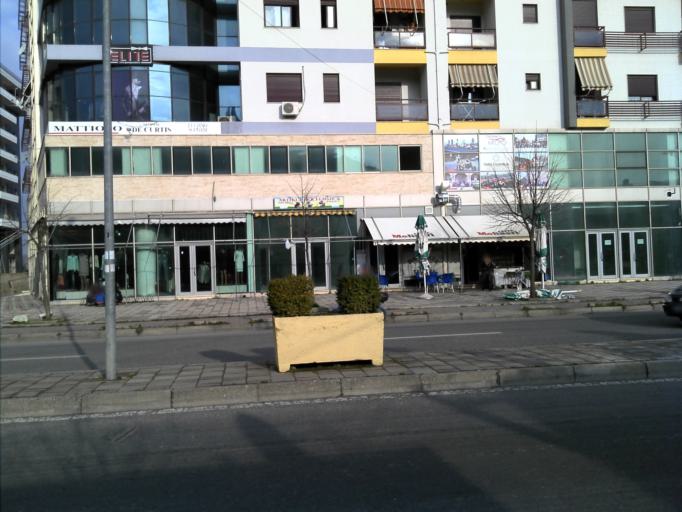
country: AL
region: Shkoder
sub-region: Rrethi i Shkodres
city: Shkoder
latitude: 42.0545
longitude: 19.4993
